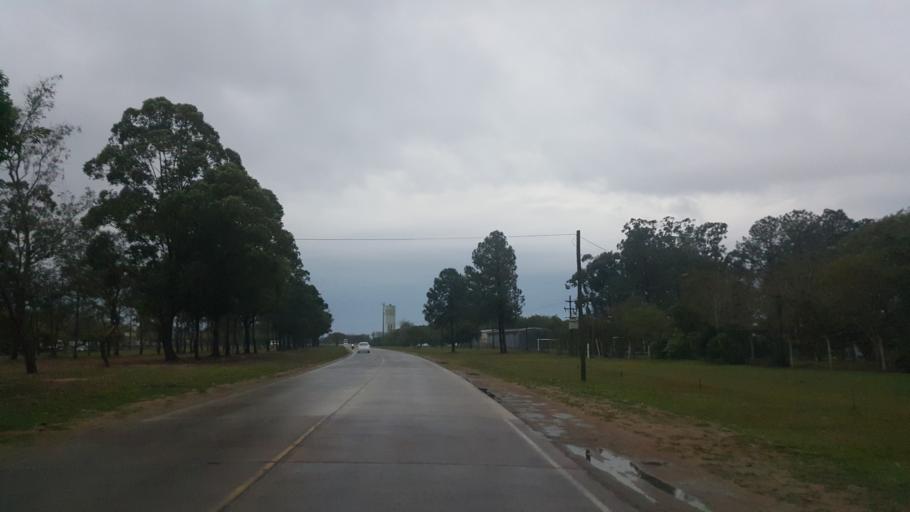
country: AR
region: Corrientes
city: Ituzaingo
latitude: -27.5828
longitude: -56.6770
